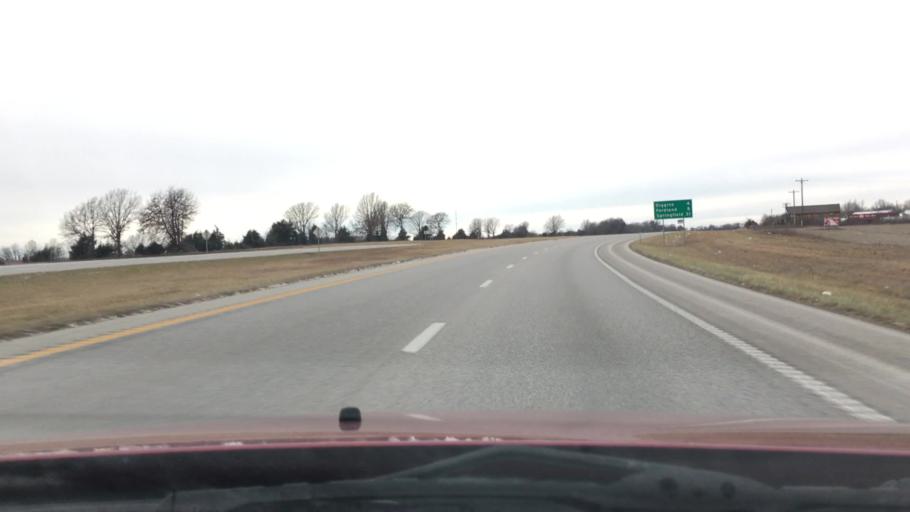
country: US
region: Missouri
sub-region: Webster County
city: Seymour
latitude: 37.1574
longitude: -92.7882
